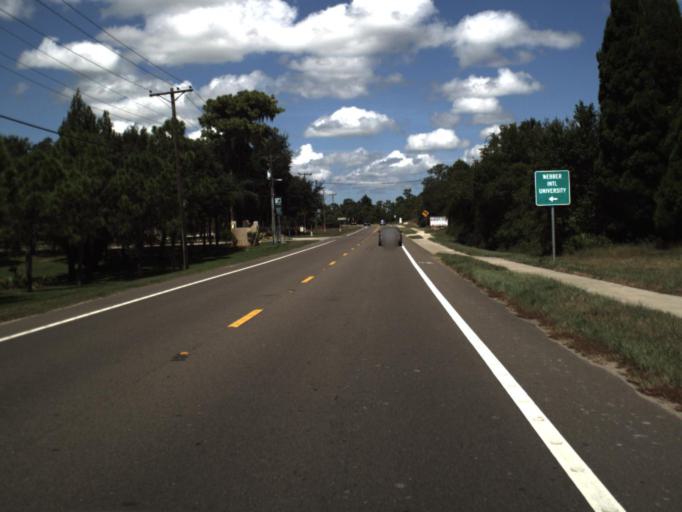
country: US
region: Florida
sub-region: Polk County
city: Babson Park
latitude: 27.8382
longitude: -81.5301
